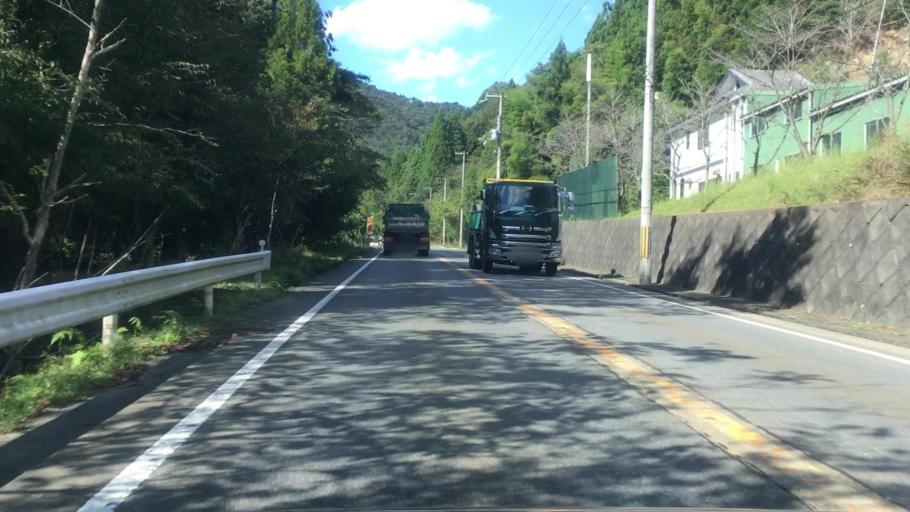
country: JP
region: Hyogo
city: Toyooka
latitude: 35.5680
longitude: 134.8527
